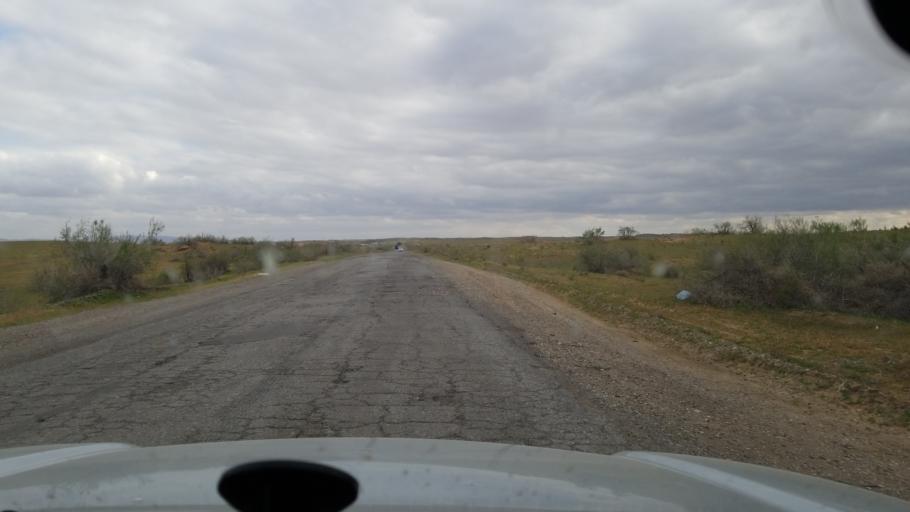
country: TM
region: Mary
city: Serhetabat
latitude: 35.9993
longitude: 62.6278
